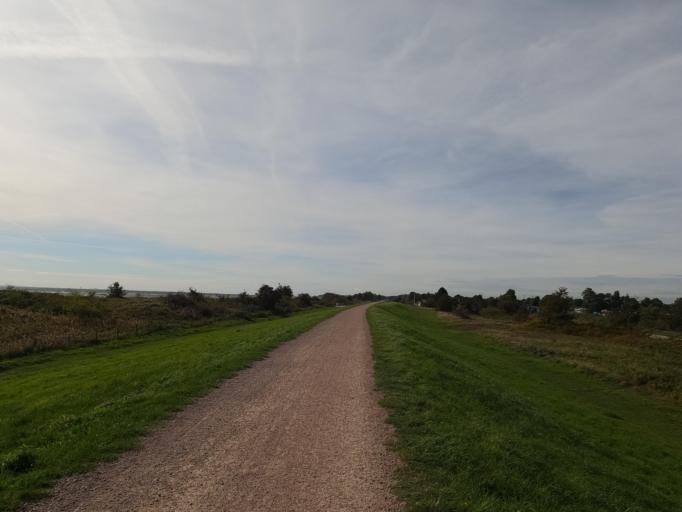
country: DE
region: Schleswig-Holstein
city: Gromitz
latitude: 54.1639
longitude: 11.0111
